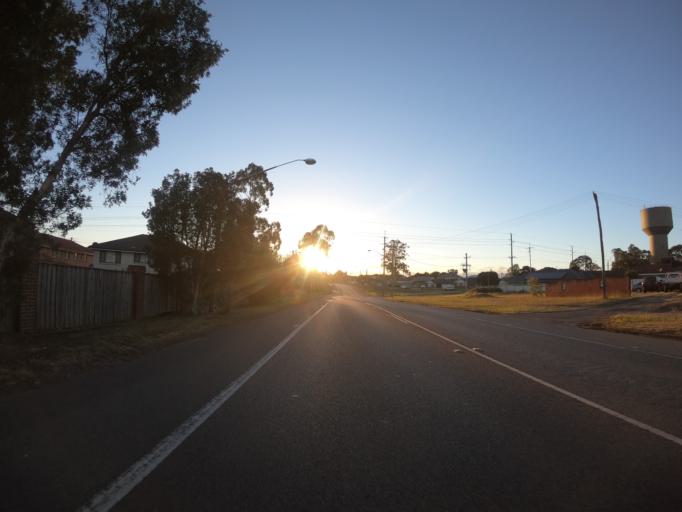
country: AU
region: New South Wales
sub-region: Hawkesbury
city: South Windsor
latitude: -33.6246
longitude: 150.7998
